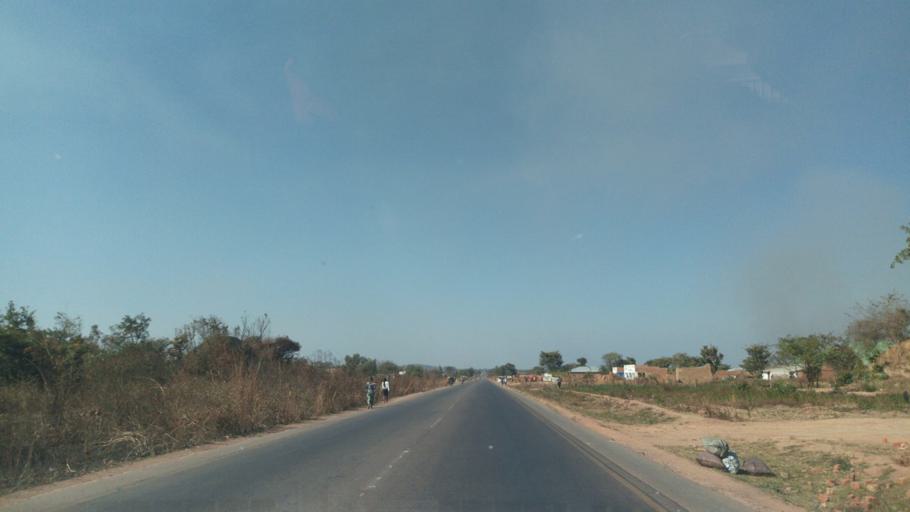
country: CD
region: Katanga
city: Lubumbashi
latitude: -11.5711
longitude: 27.5450
